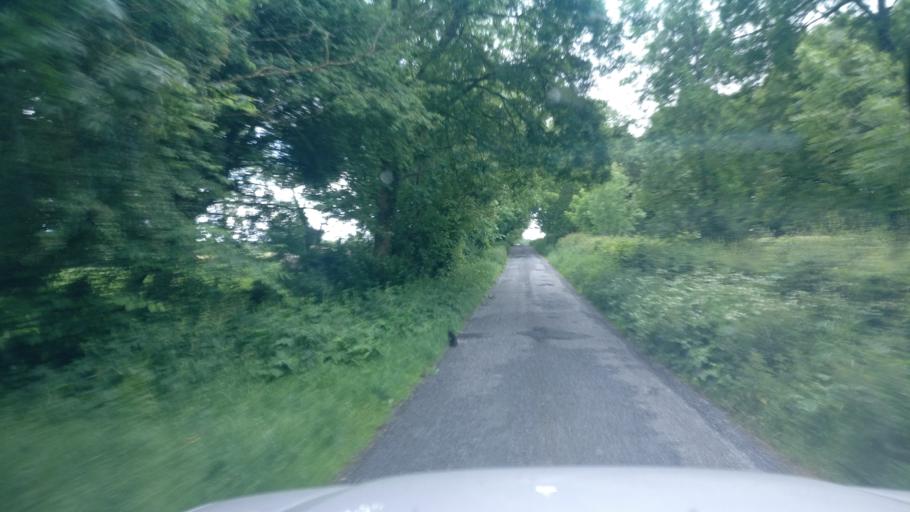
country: IE
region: Connaught
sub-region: County Galway
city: Ballinasloe
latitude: 53.2313
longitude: -8.2163
